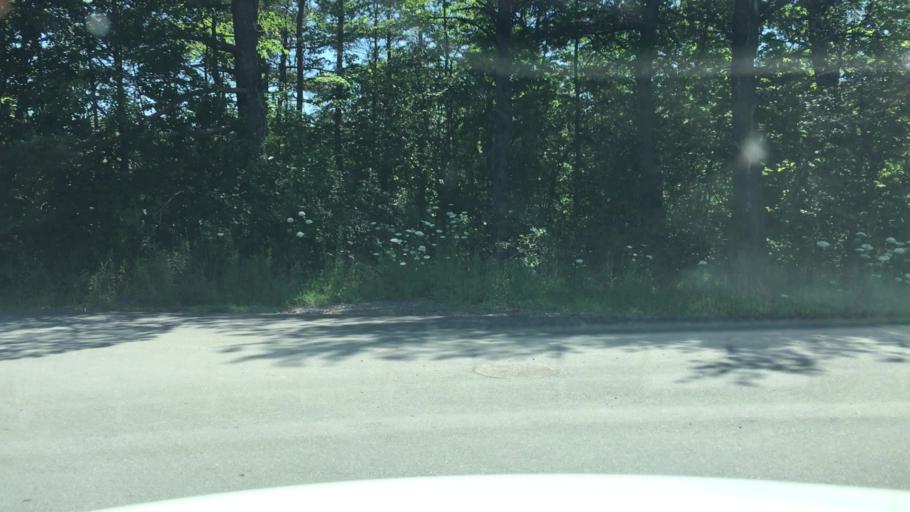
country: US
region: Maine
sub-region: Penobscot County
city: Bangor
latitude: 44.8073
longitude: -68.7958
